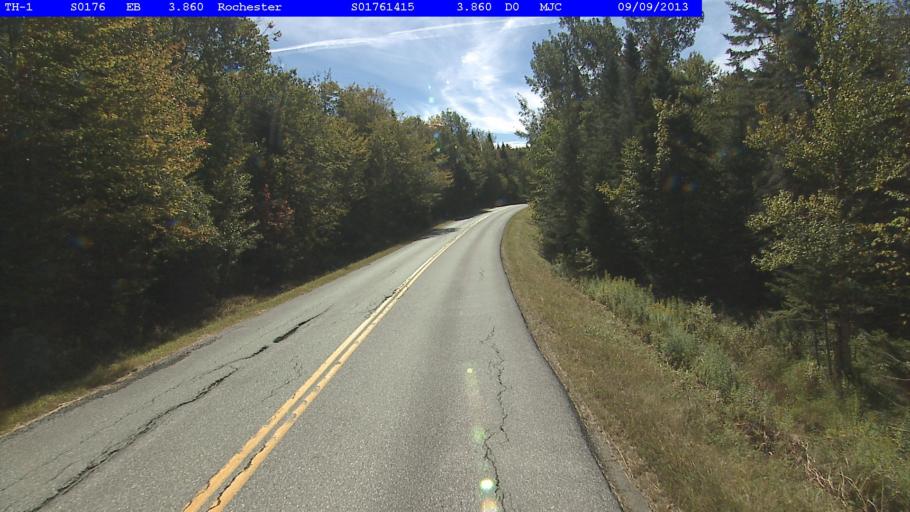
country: US
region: Vermont
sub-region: Orange County
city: Randolph
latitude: 43.8524
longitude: -72.7521
